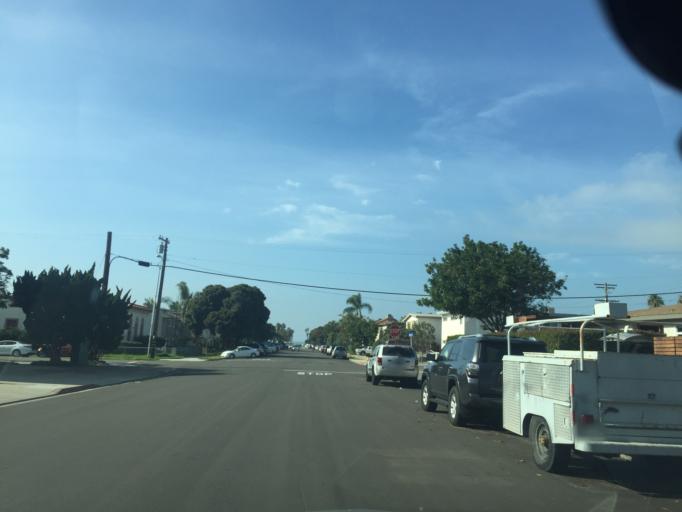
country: US
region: California
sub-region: San Diego County
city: La Jolla
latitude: 32.7970
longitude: -117.2492
